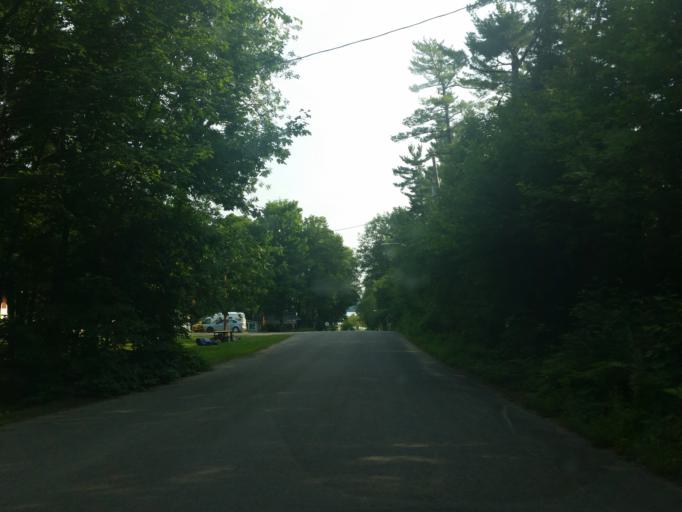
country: CA
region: Quebec
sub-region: Outaouais
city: Shawville
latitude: 45.5205
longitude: -76.4274
